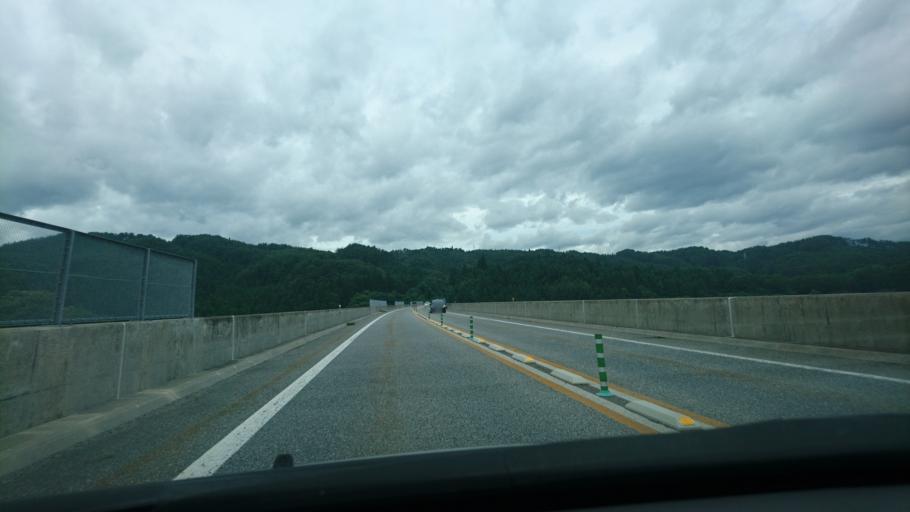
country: JP
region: Iwate
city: Yamada
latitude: 39.4592
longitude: 141.9420
